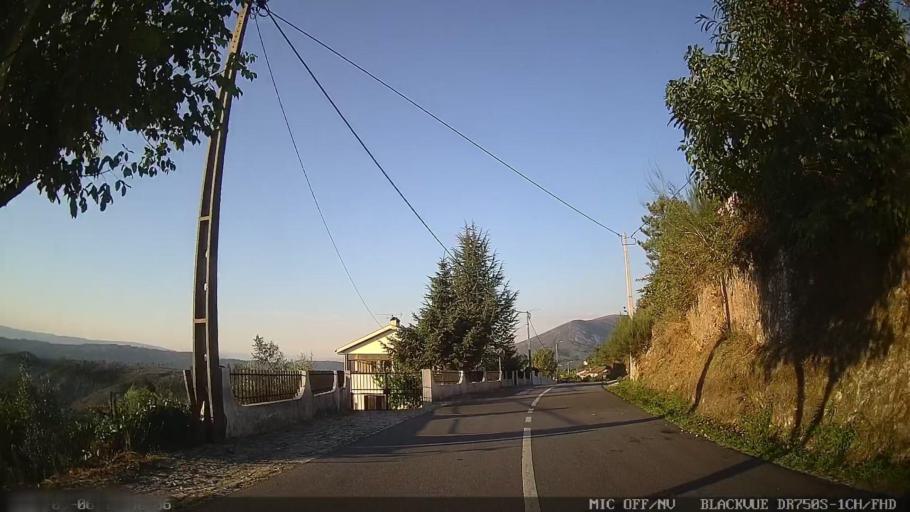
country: PT
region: Porto
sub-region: Baiao
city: Baiao
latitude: 41.2399
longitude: -7.9977
